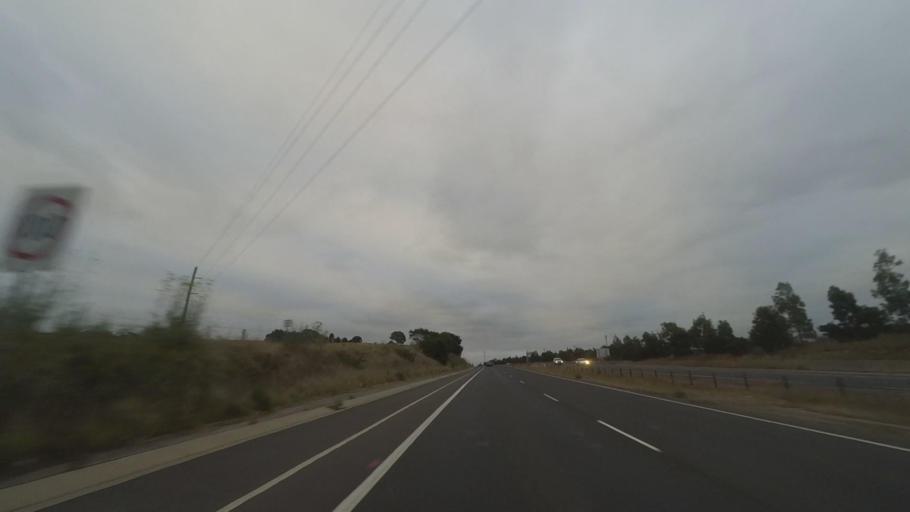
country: AU
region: New South Wales
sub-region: Shellharbour
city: Croom
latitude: -34.5807
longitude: 150.8359
